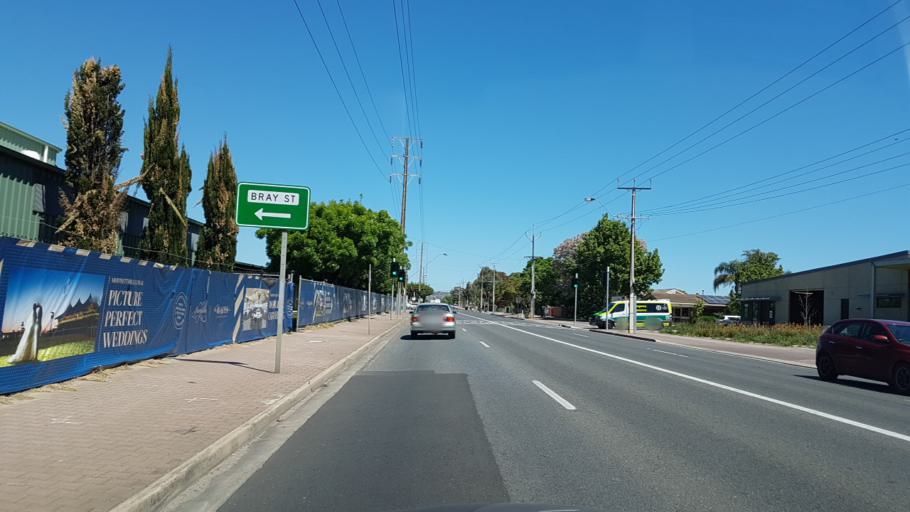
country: AU
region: South Australia
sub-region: Marion
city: Plympton Park
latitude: -34.9800
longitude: 138.5381
